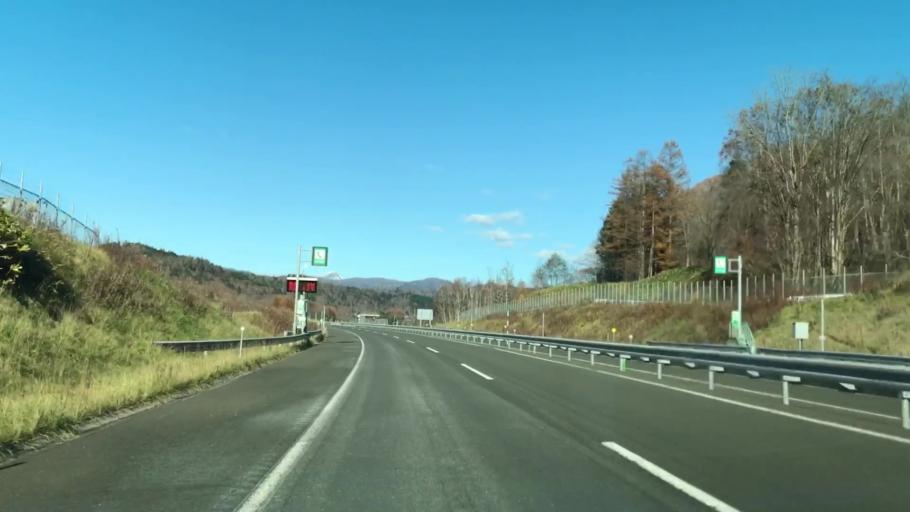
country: JP
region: Hokkaido
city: Shimo-furano
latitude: 42.9257
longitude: 142.2033
